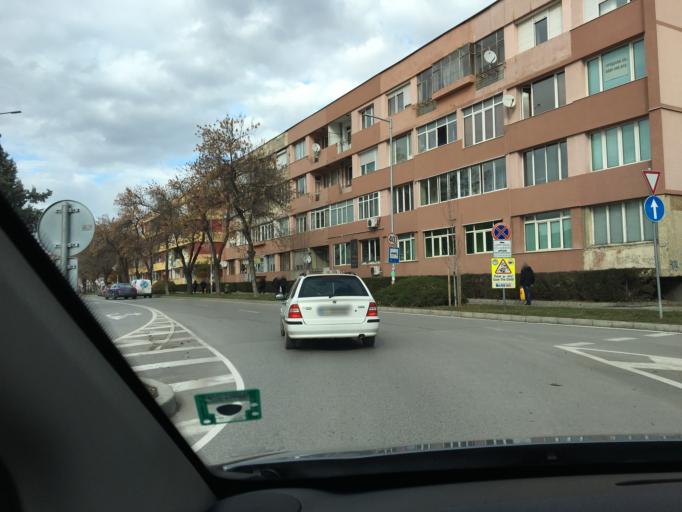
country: BG
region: Blagoevgrad
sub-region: Obshtina Blagoevgrad
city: Blagoevgrad
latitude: 42.0173
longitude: 23.0945
